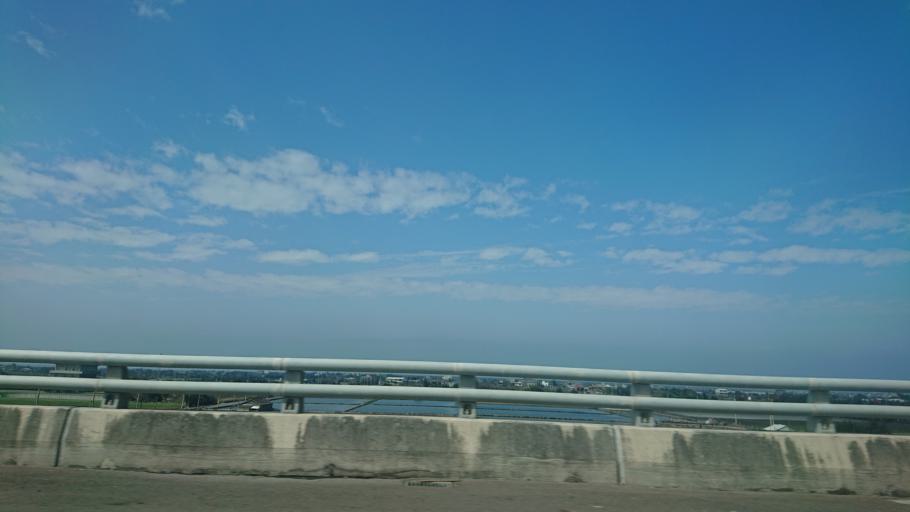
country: TW
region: Taiwan
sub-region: Yunlin
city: Douliu
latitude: 23.8447
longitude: 120.2937
